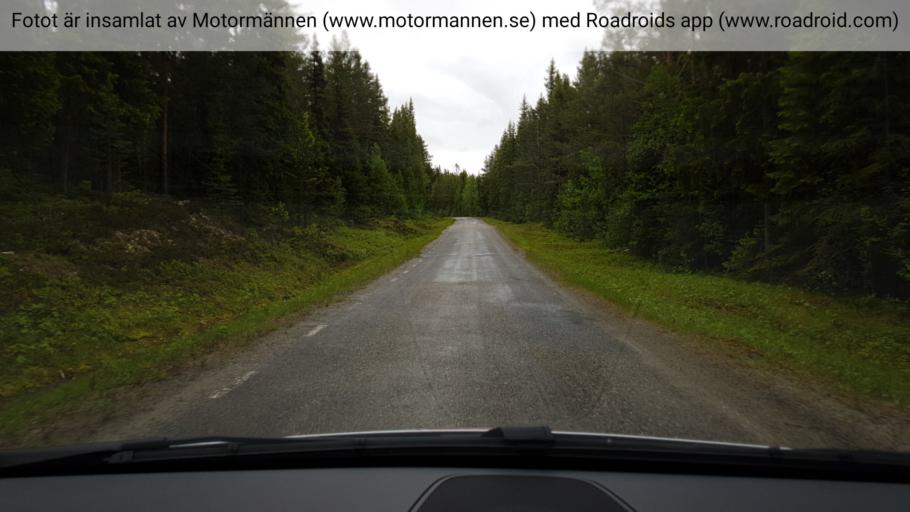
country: SE
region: Jaemtland
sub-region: Harjedalens Kommun
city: Sveg
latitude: 62.2441
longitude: 13.3637
